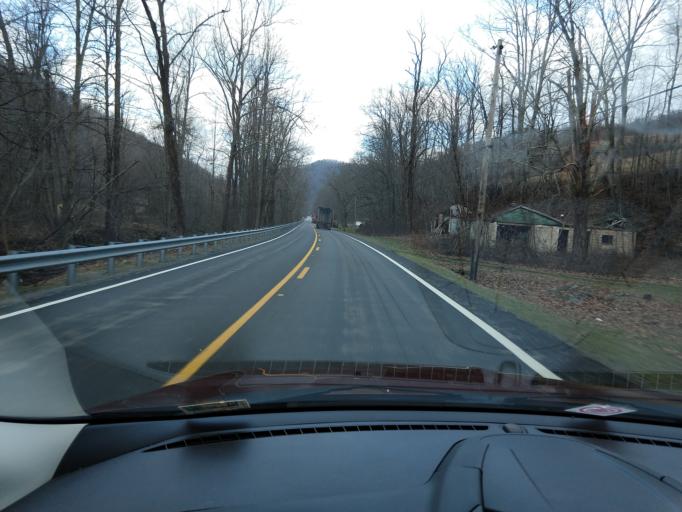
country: US
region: West Virginia
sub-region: Randolph County
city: Elkins
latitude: 38.6650
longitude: -79.9396
